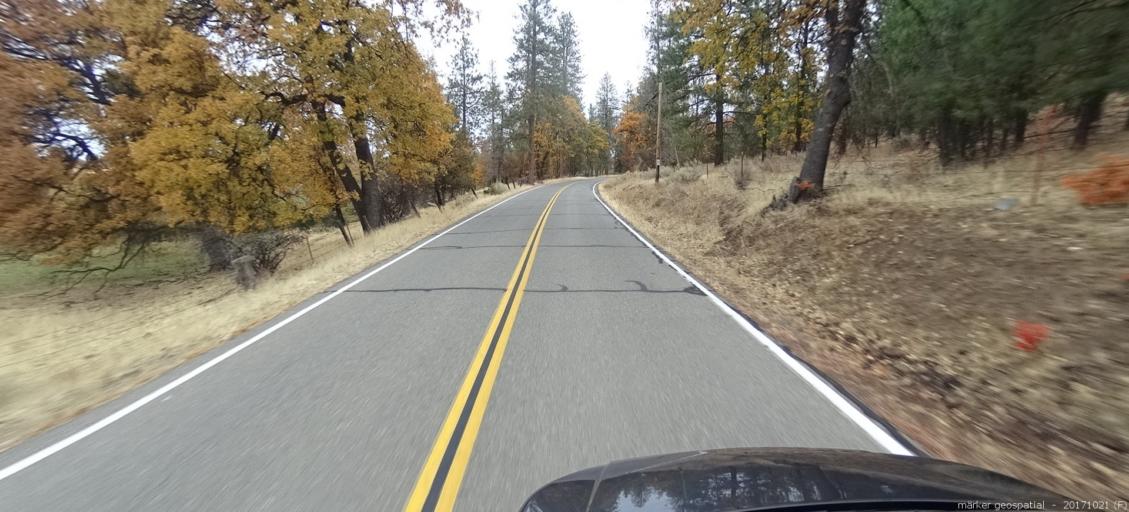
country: US
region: California
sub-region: Shasta County
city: Burney
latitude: 41.0012
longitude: -121.4322
